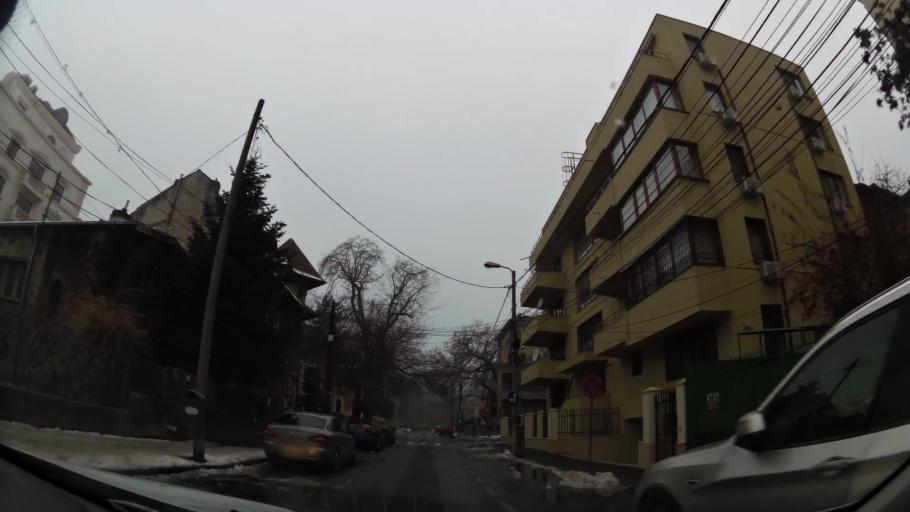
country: RO
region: Bucuresti
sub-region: Municipiul Bucuresti
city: Bucuresti
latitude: 44.4652
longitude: 26.0838
